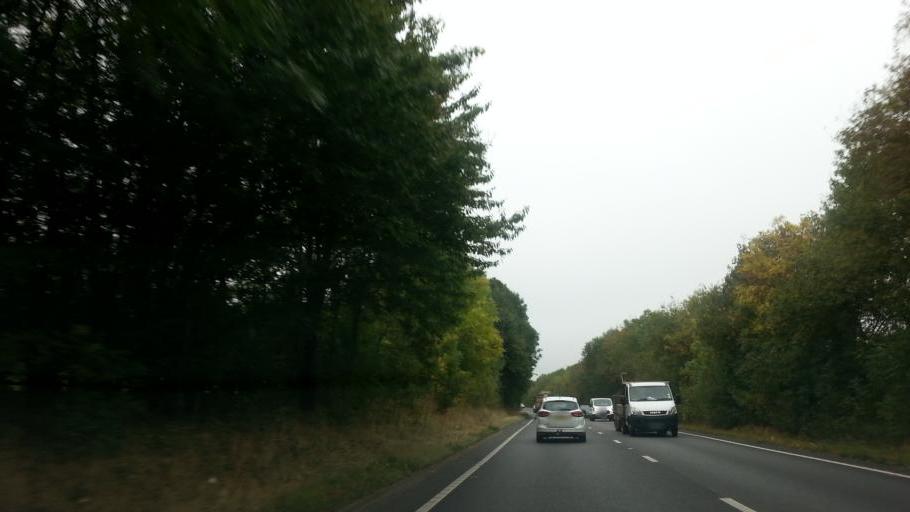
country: GB
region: England
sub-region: Northamptonshire
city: Stanwick
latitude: 52.3482
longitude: -0.5617
